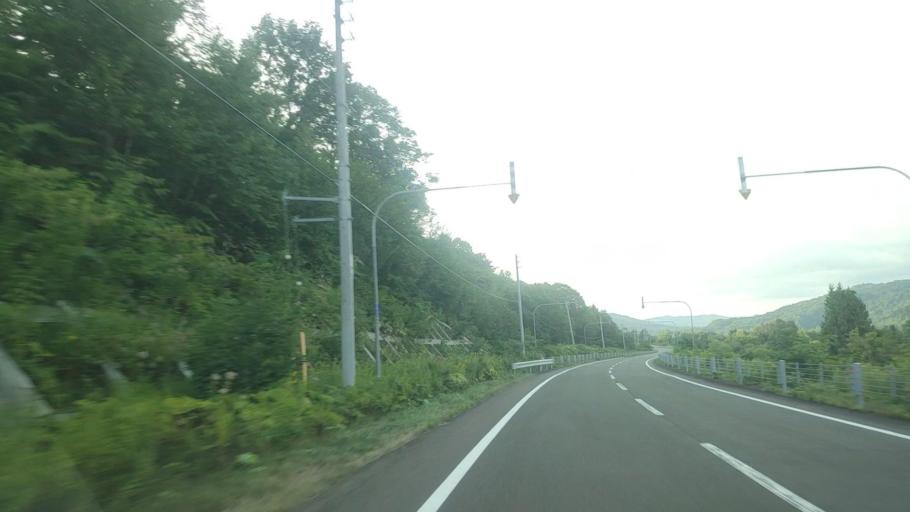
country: JP
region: Hokkaido
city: Bibai
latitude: 43.0744
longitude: 142.1024
